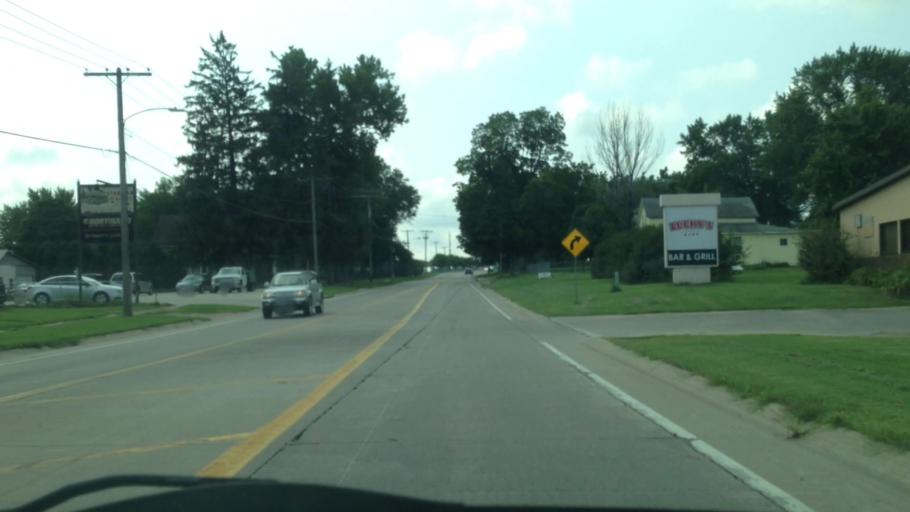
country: US
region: Iowa
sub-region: Linn County
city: Fairfax
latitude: 41.9177
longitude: -91.7837
